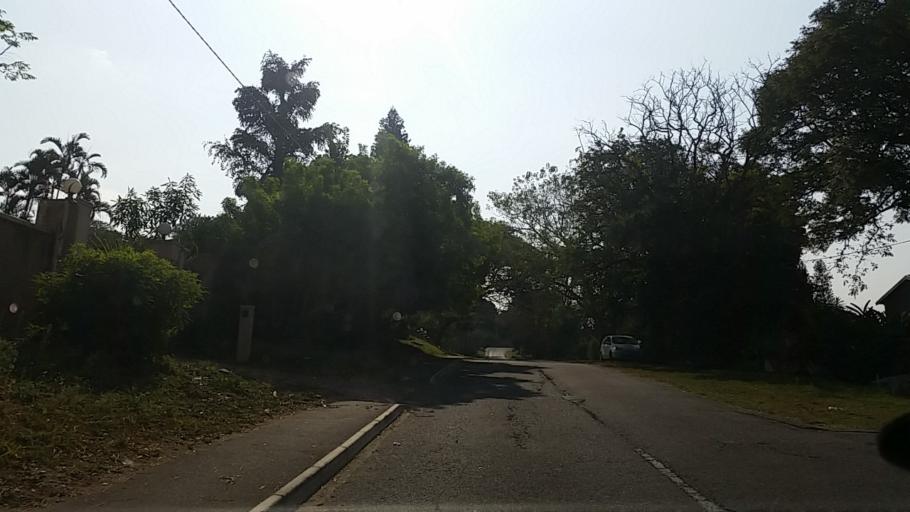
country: ZA
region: KwaZulu-Natal
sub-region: eThekwini Metropolitan Municipality
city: Berea
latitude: -29.8433
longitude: 30.9405
